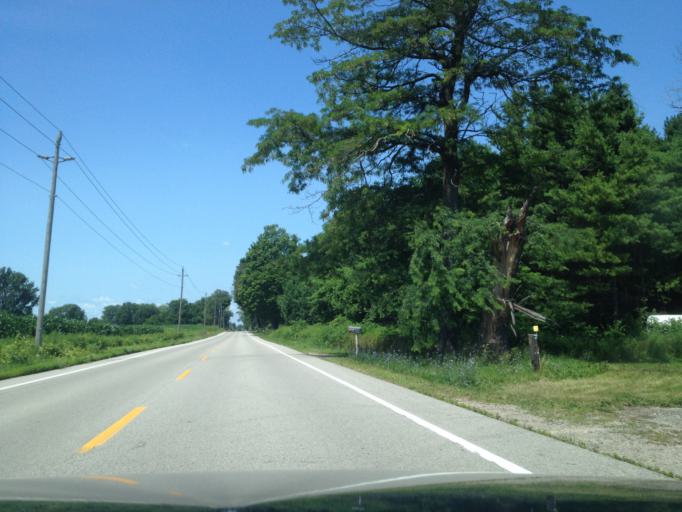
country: CA
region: Ontario
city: Norfolk County
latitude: 42.5878
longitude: -80.6244
